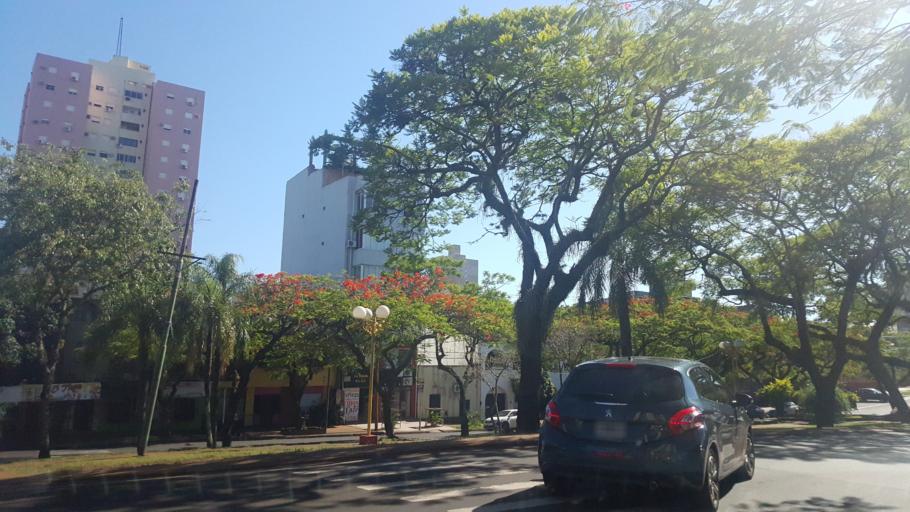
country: AR
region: Misiones
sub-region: Departamento de Capital
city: Posadas
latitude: -27.3610
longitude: -55.8980
